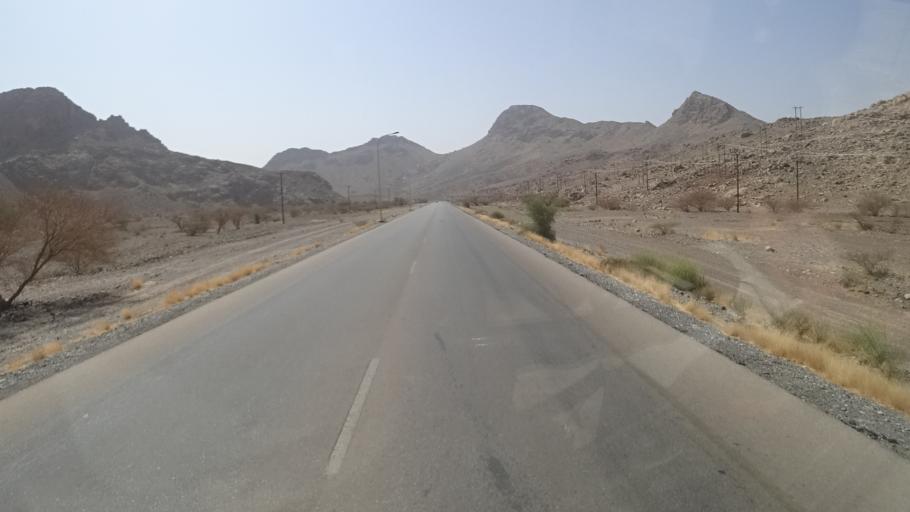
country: OM
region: Muhafazat ad Dakhiliyah
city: Bahla'
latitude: 23.0421
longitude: 57.3137
